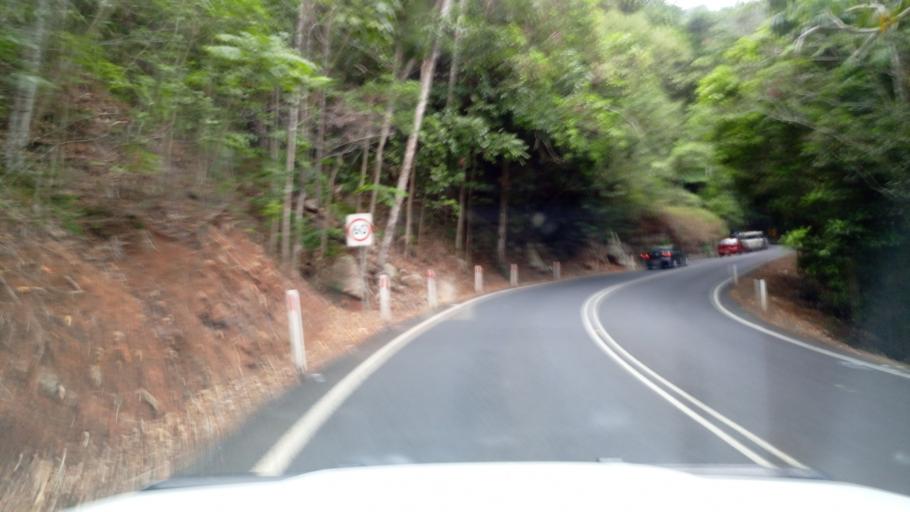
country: AU
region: Queensland
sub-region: Cairns
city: Redlynch
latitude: -16.8468
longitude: 145.6754
